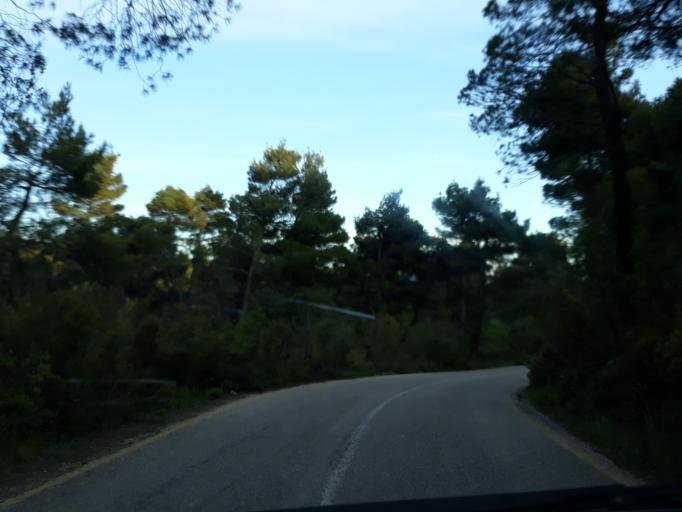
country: GR
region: Attica
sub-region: Nomarchia Anatolikis Attikis
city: Afidnes
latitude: 38.2113
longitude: 23.7900
